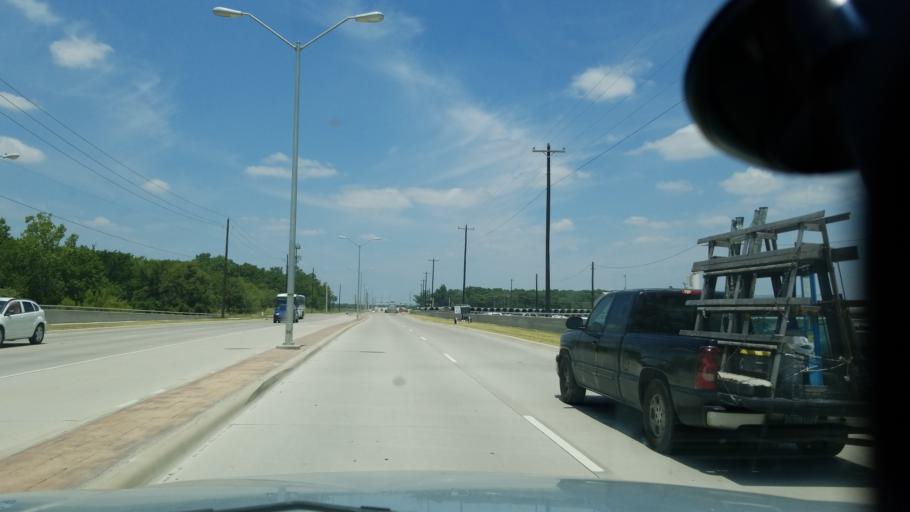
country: US
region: Texas
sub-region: Dallas County
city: Grand Prairie
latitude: 32.7671
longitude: -96.9600
